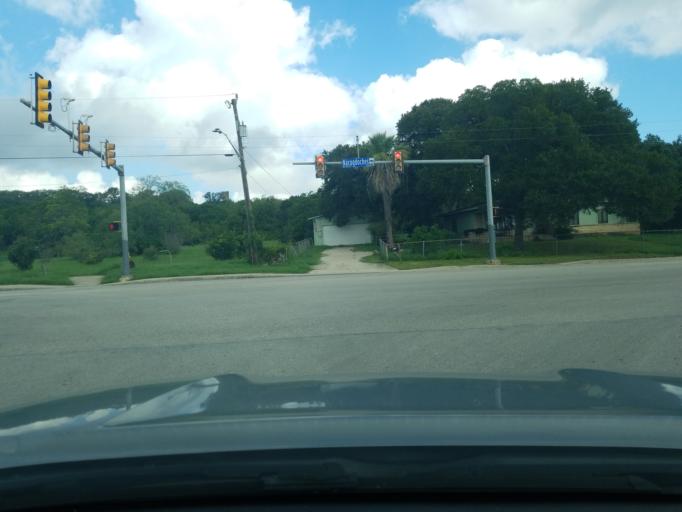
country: US
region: Texas
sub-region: Bexar County
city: Live Oak
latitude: 29.5832
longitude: -98.3653
